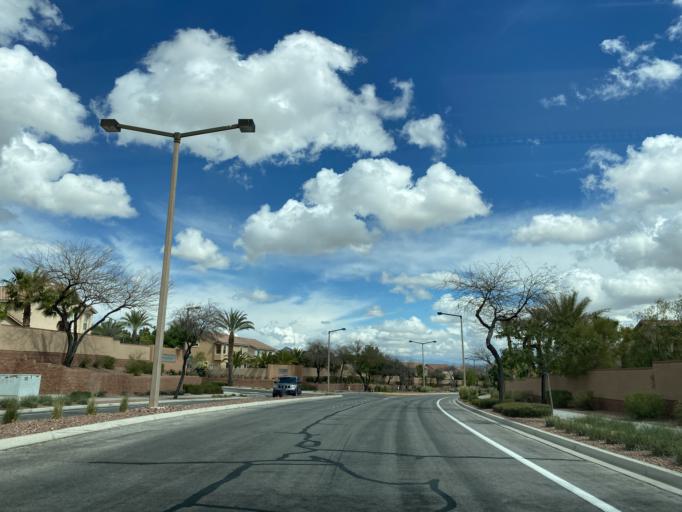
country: US
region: Nevada
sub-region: Clark County
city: Summerlin South
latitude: 36.1861
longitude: -115.3390
